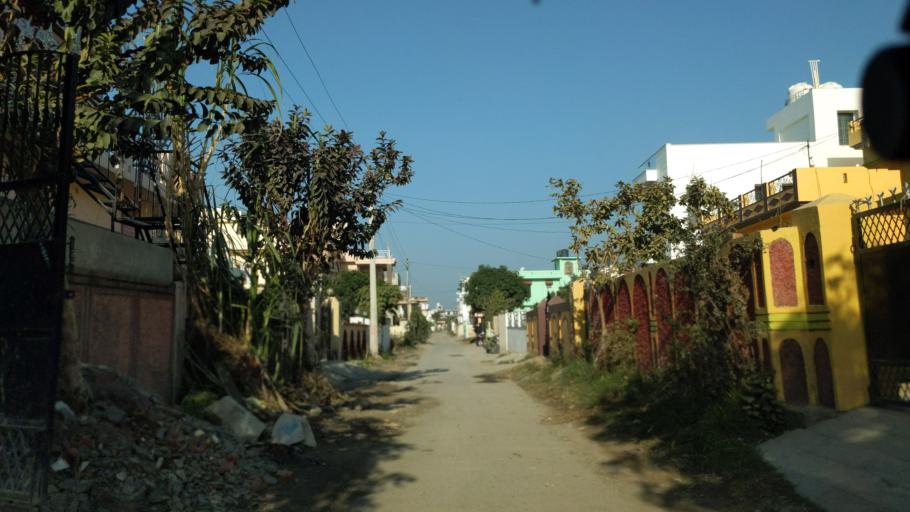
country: IN
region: Uttarakhand
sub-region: Naini Tal
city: Haldwani
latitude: 29.2064
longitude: 79.4977
